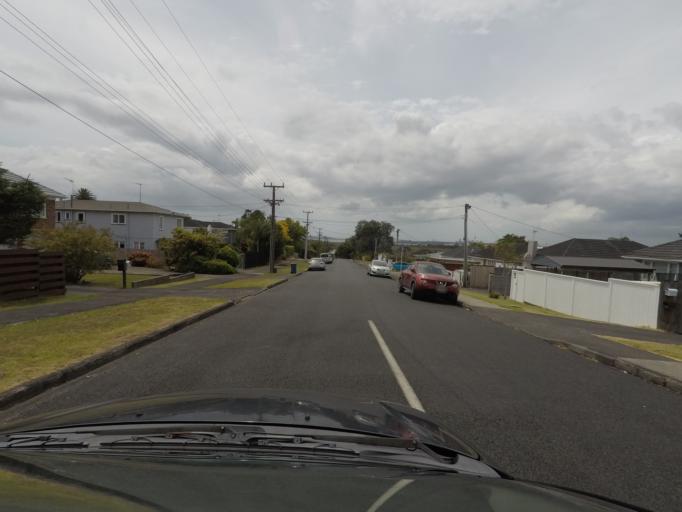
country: NZ
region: Auckland
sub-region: Auckland
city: Rosebank
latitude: -36.8701
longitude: 174.6534
